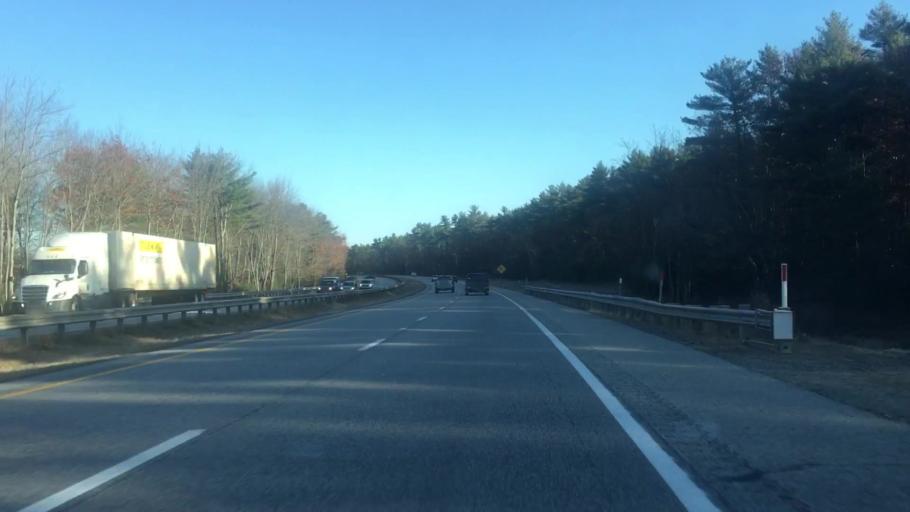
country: US
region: Maine
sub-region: Cumberland County
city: New Gloucester
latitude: 43.9787
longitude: -70.3136
